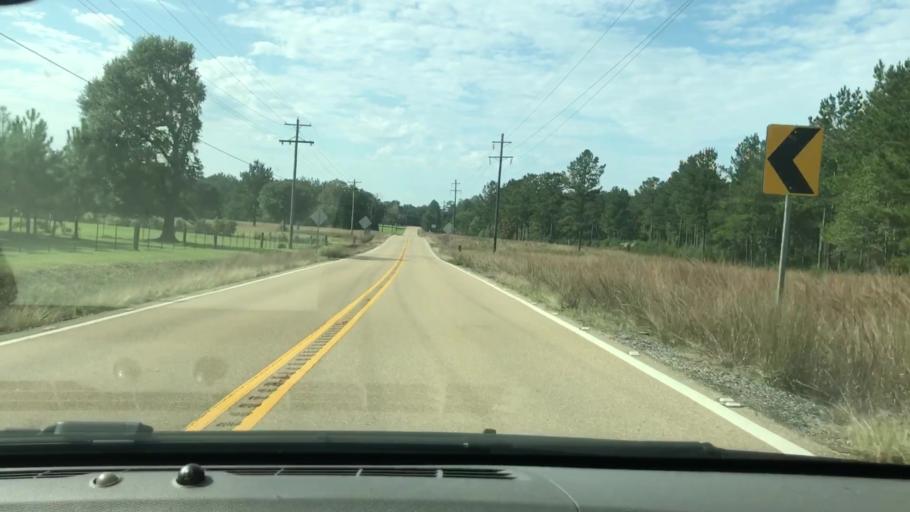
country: US
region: Louisiana
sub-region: Saint Tammany Parish
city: Abita Springs
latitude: 30.5214
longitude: -89.9337
